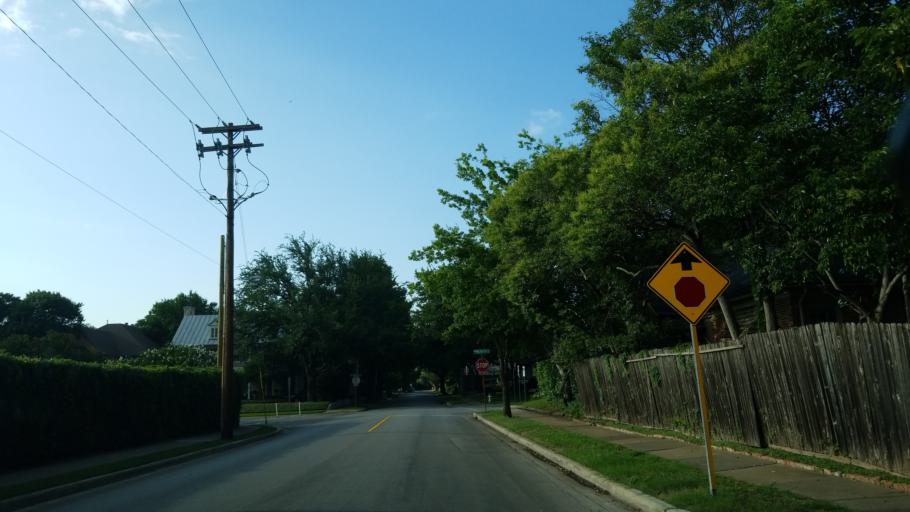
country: US
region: Texas
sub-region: Dallas County
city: University Park
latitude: 32.8434
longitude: -96.7955
